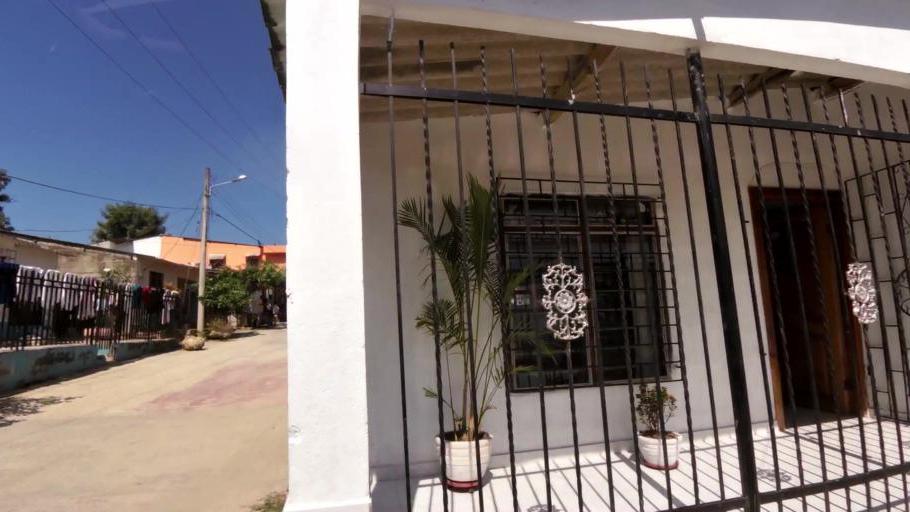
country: CO
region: Bolivar
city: Cartagena
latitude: 10.3558
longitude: -75.4898
